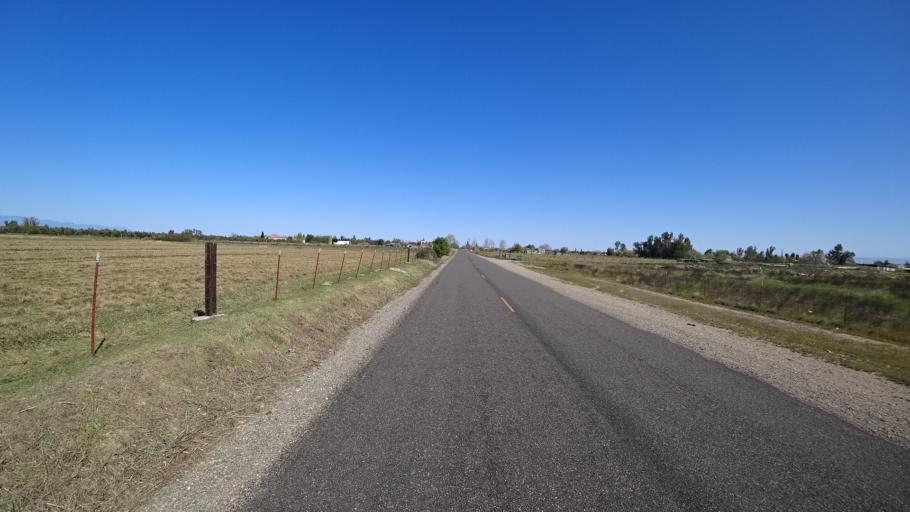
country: US
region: California
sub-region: Glenn County
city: Orland
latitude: 39.7287
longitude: -122.2158
